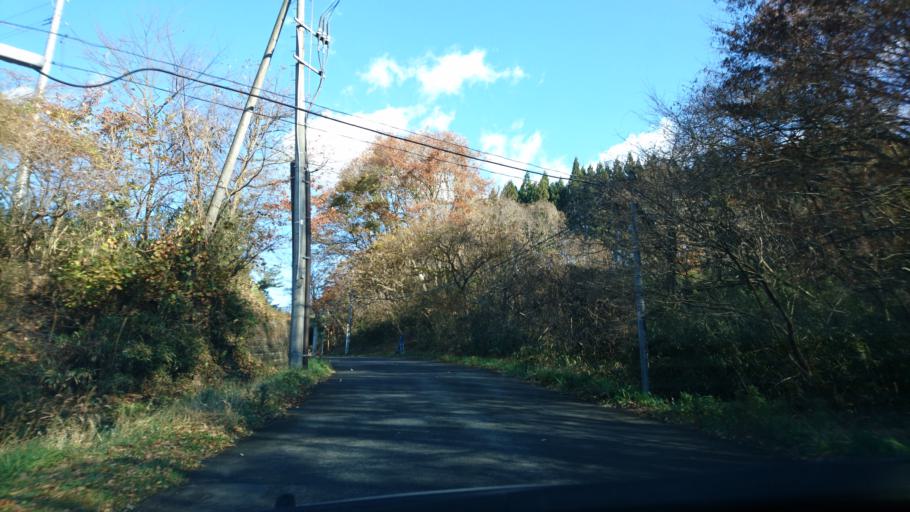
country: JP
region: Iwate
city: Ichinoseki
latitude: 38.9996
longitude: 141.0892
